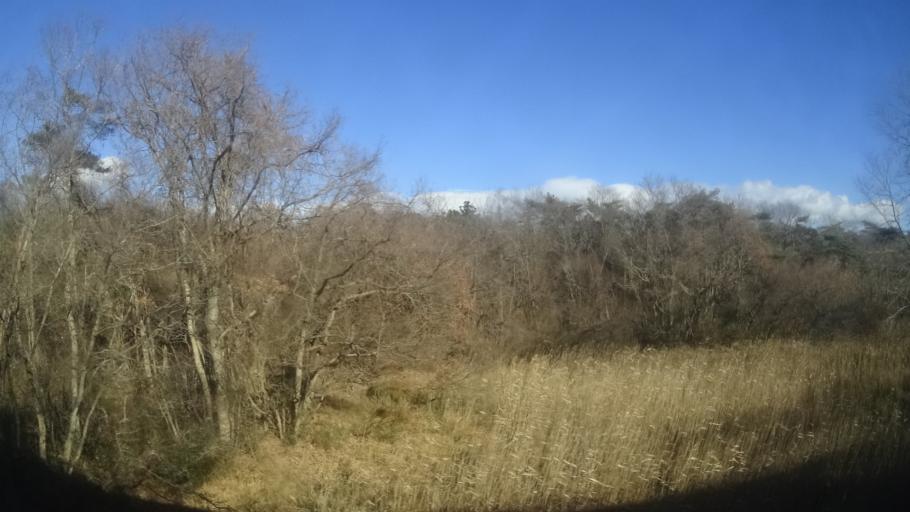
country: JP
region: Miyagi
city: Marumori
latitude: 37.7391
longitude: 140.9471
